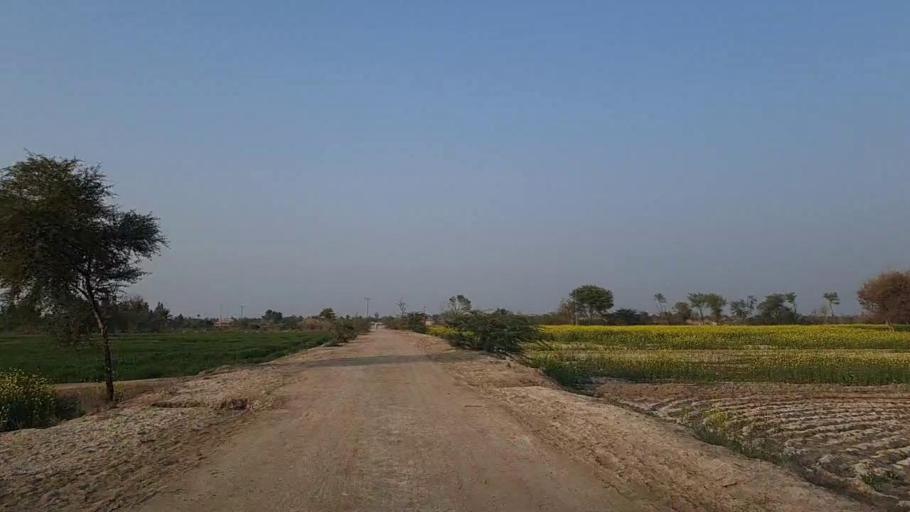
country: PK
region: Sindh
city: Daur
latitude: 26.4080
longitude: 68.3829
